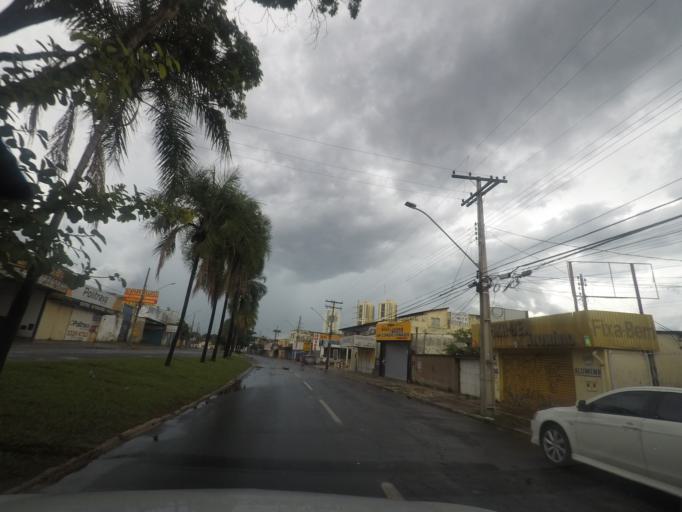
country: BR
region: Goias
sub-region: Goiania
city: Goiania
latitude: -16.6690
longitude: -49.2741
